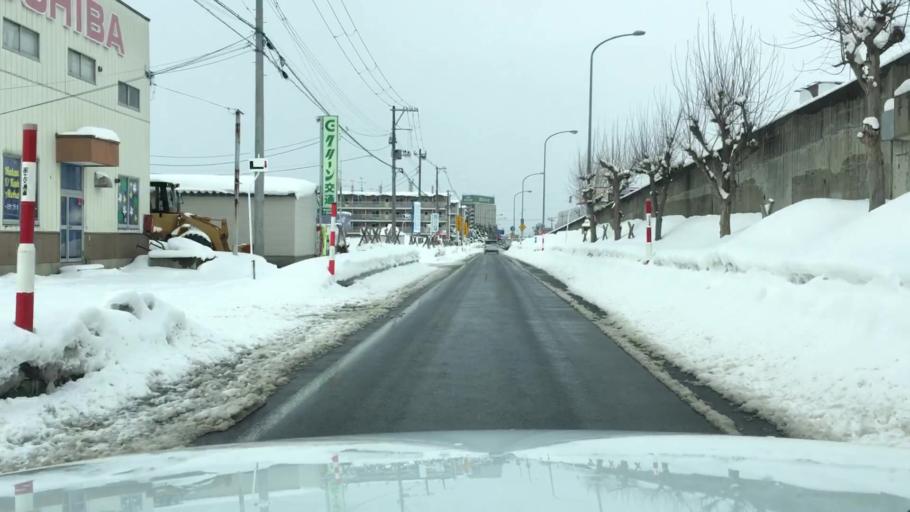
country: JP
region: Aomori
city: Hirosaki
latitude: 40.5978
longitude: 140.5023
